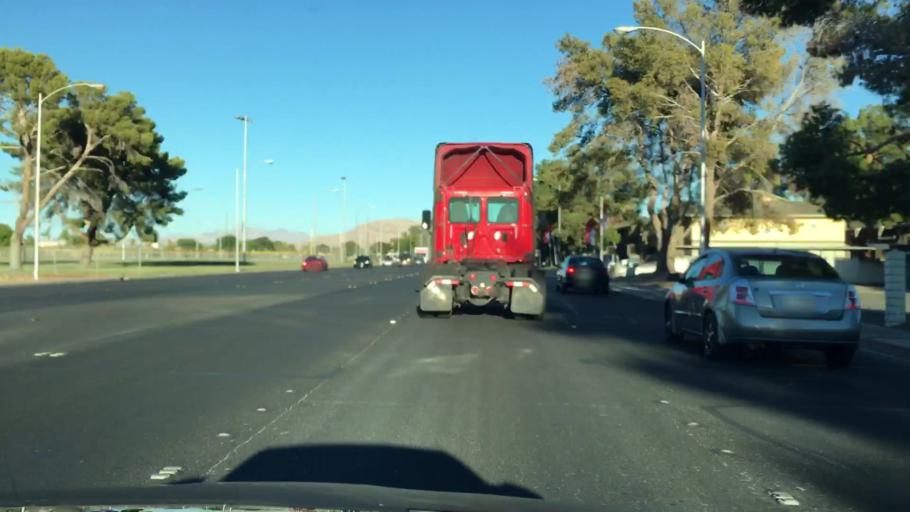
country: US
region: Nevada
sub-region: Clark County
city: North Las Vegas
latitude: 36.2176
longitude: -115.1037
